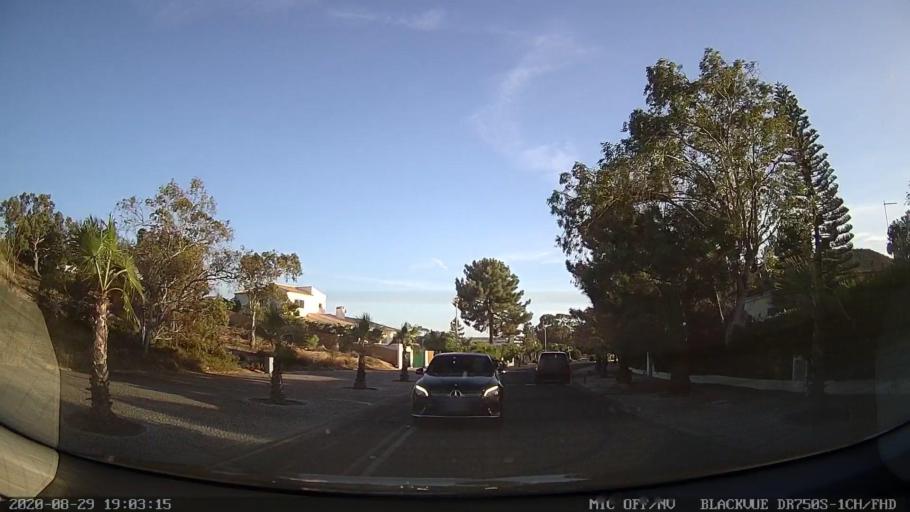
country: PT
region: Setubal
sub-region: Setubal
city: Setubal
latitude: 38.4546
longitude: -8.8576
